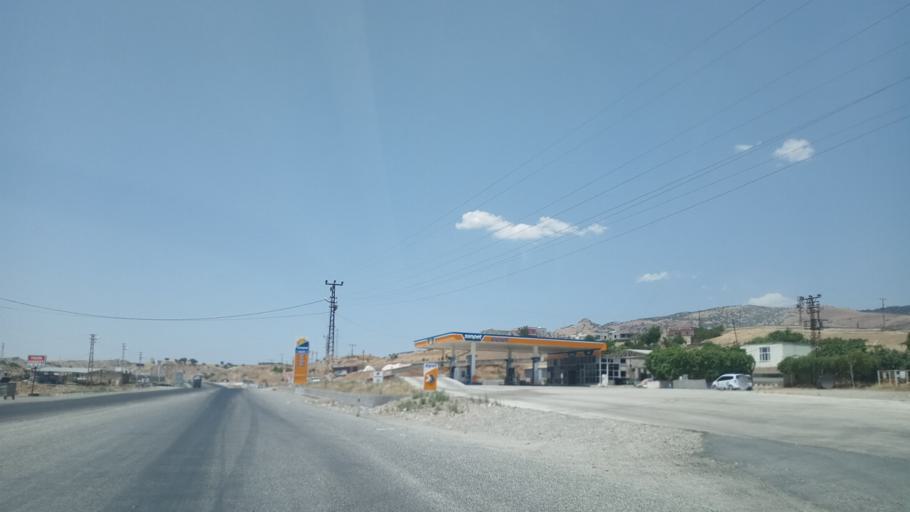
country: TR
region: Batman
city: Kozluk
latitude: 38.1682
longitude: 41.4884
